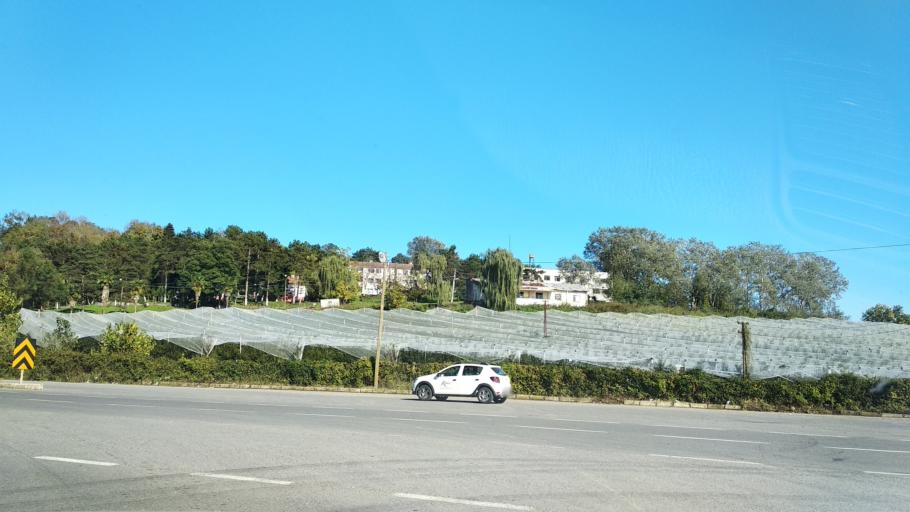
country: TR
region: Sakarya
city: Ortakoy
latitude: 41.0330
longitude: 30.6168
